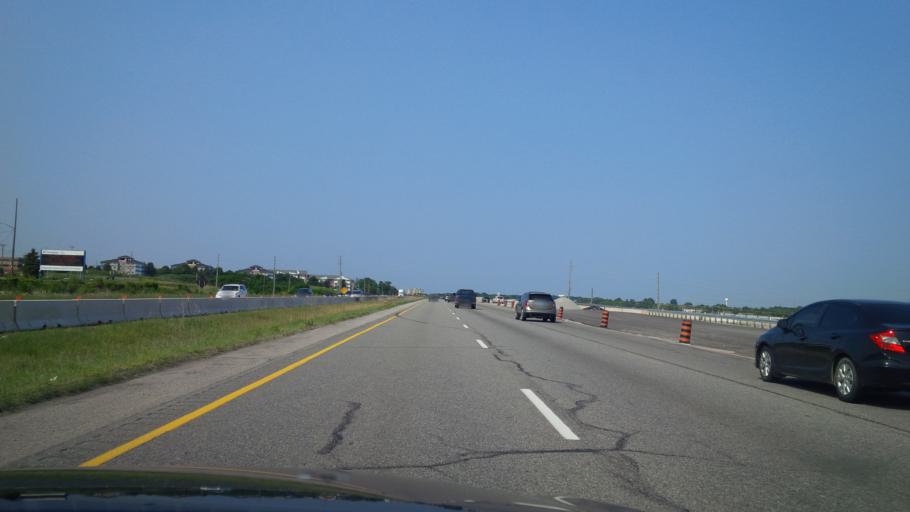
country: CA
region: Ontario
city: Barrie
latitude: 44.4150
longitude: -79.6693
